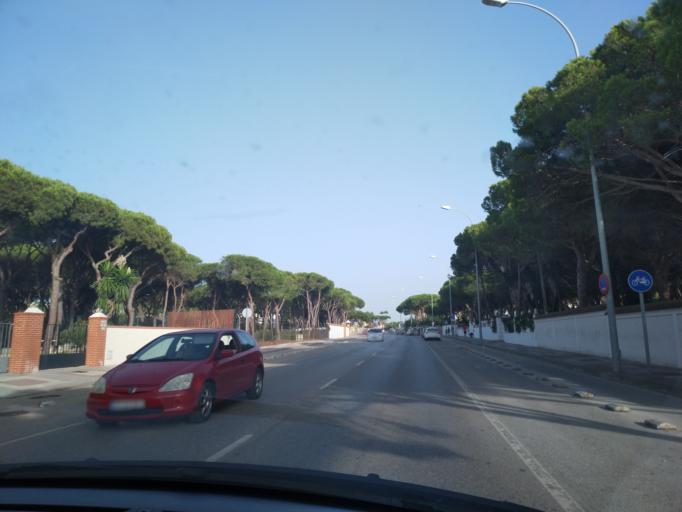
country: ES
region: Andalusia
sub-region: Provincia de Cadiz
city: Chiclana de la Frontera
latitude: 36.3783
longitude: -6.1891
